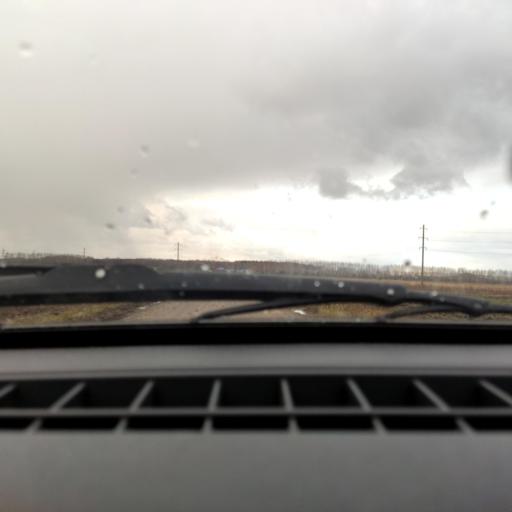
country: RU
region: Bashkortostan
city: Iglino
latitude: 54.7410
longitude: 56.3220
